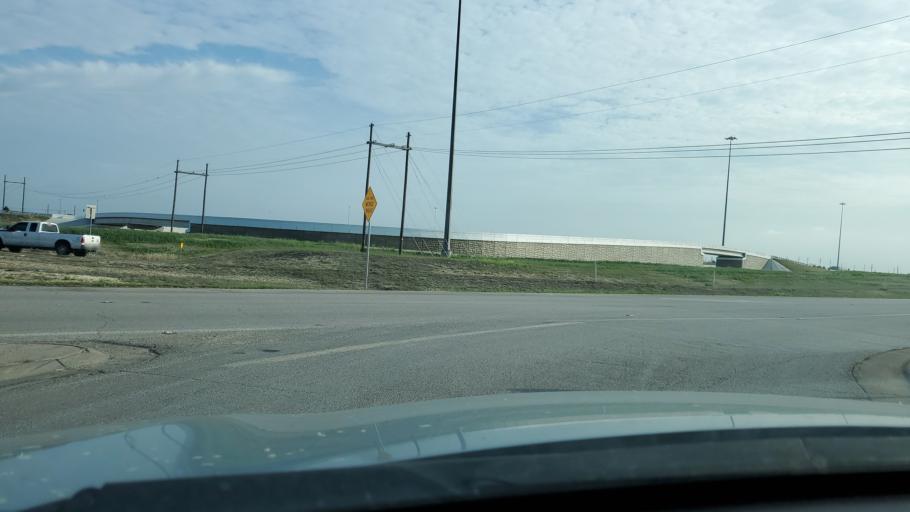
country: US
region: Texas
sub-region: Bell County
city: Fort Hood
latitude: 31.1203
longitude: -97.7979
